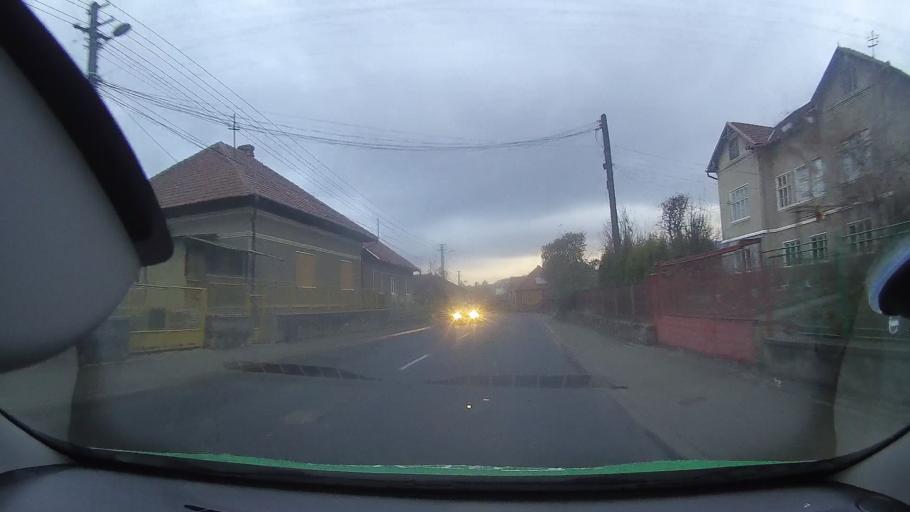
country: RO
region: Hunedoara
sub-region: Municipiul Brad
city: Brad
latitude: 46.1329
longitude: 22.7835
